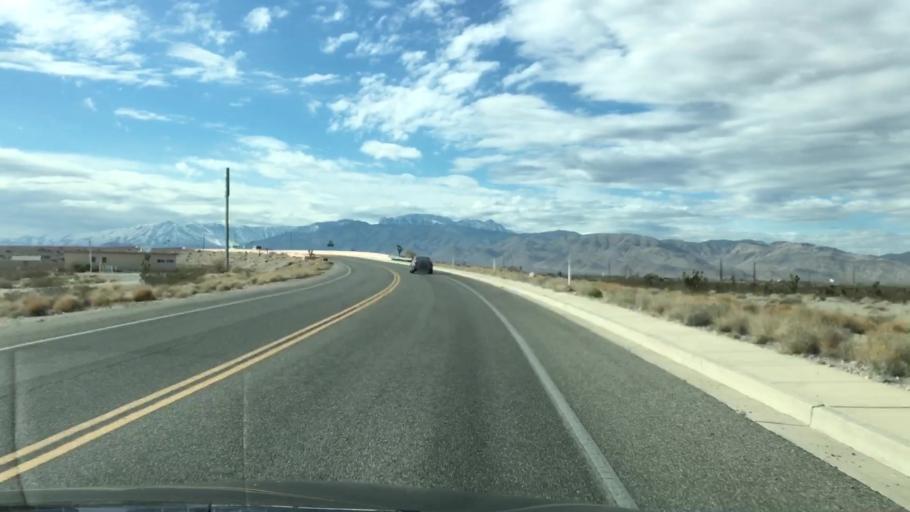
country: US
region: Nevada
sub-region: Clark County
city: Summerlin South
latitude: 36.3642
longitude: -115.3471
